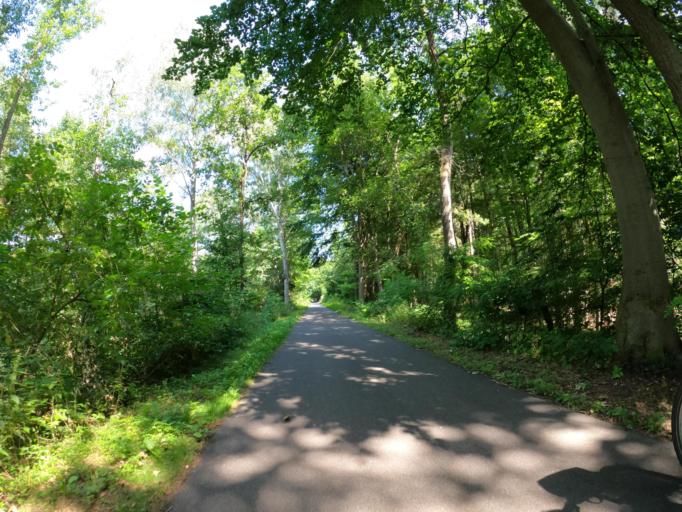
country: DE
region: Brandenburg
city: Templin
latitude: 53.2338
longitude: 13.5021
